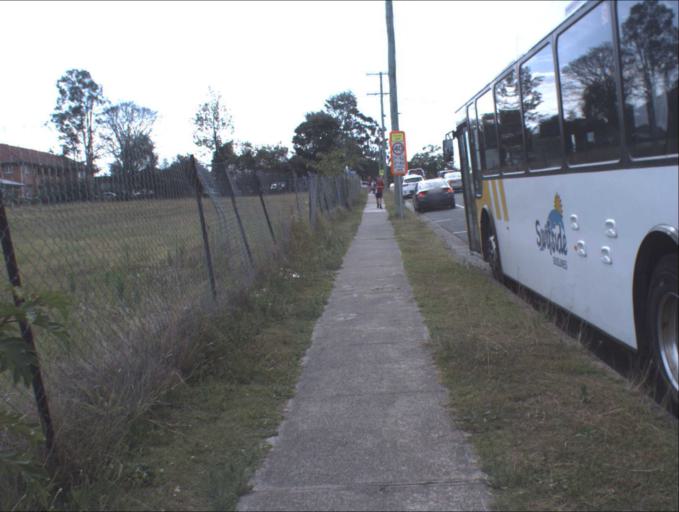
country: AU
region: Queensland
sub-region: Logan
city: Beenleigh
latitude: -27.7119
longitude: 153.2016
